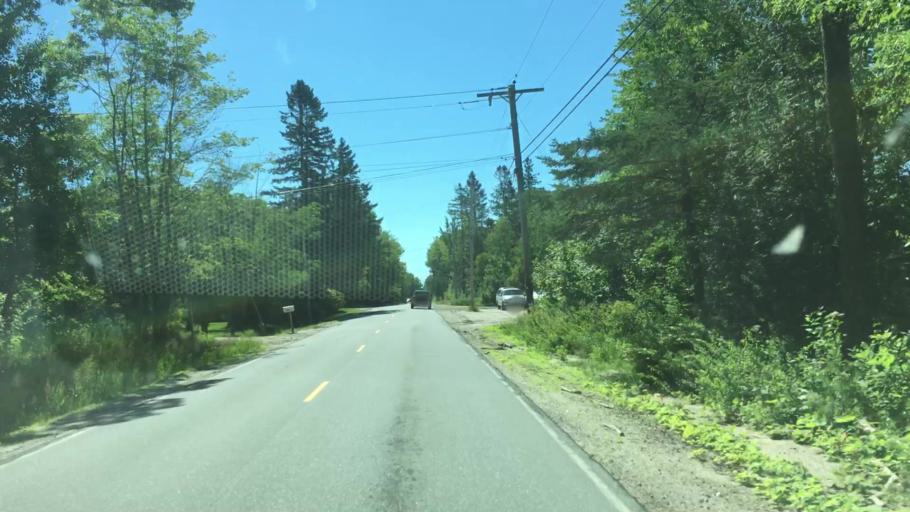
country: US
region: Maine
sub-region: Hancock County
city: Penobscot
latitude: 44.4176
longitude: -68.6132
